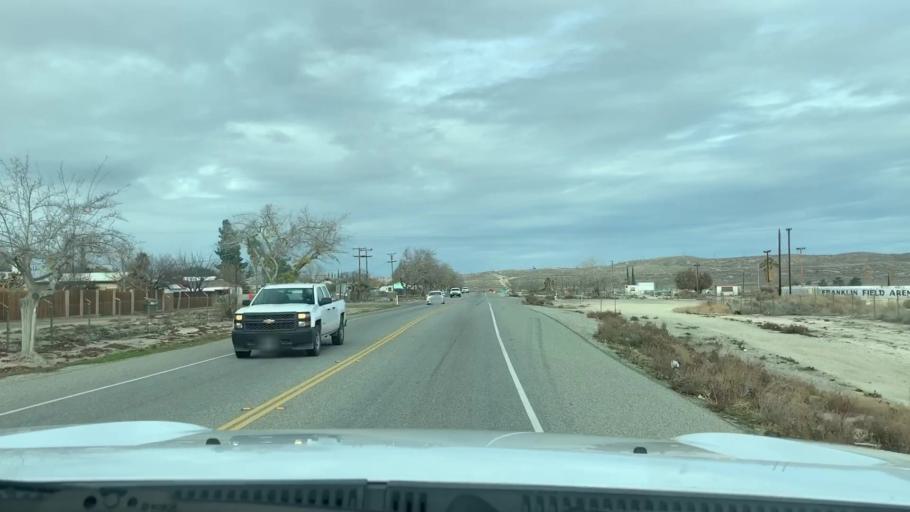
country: US
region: California
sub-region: Kern County
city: Ford City
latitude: 35.1505
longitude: -119.4478
